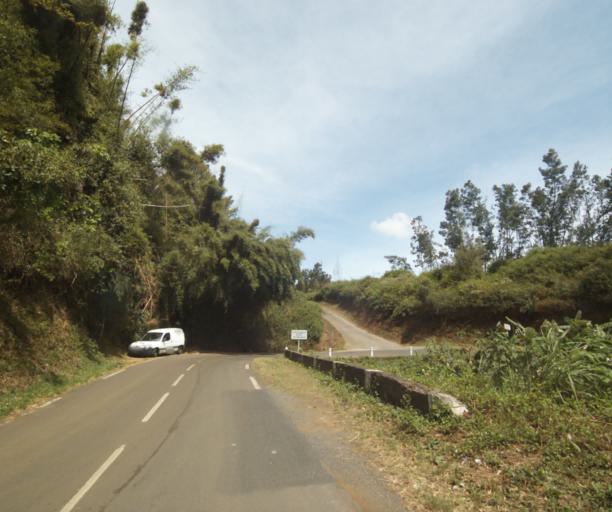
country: RE
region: Reunion
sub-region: Reunion
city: Trois-Bassins
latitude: -21.0674
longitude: 55.3091
